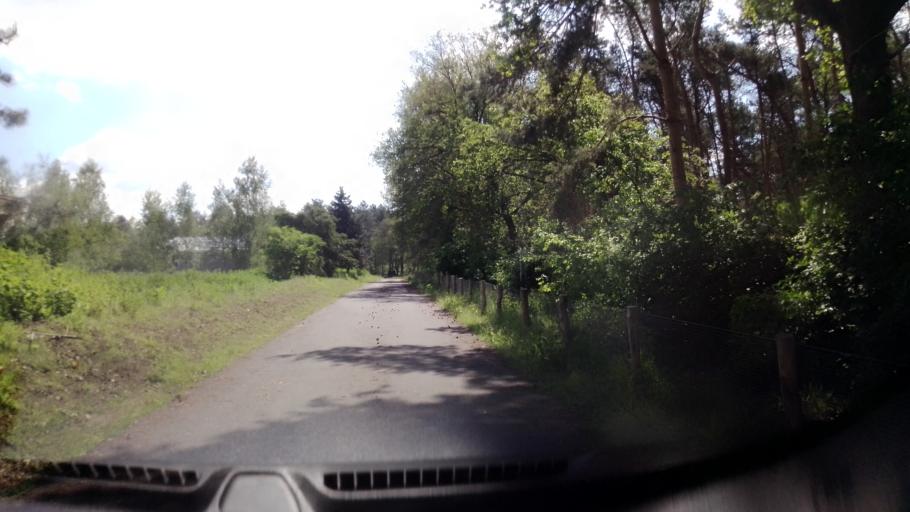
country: NL
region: Limburg
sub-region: Gemeente Venlo
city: Venlo
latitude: 51.4057
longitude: 6.1203
